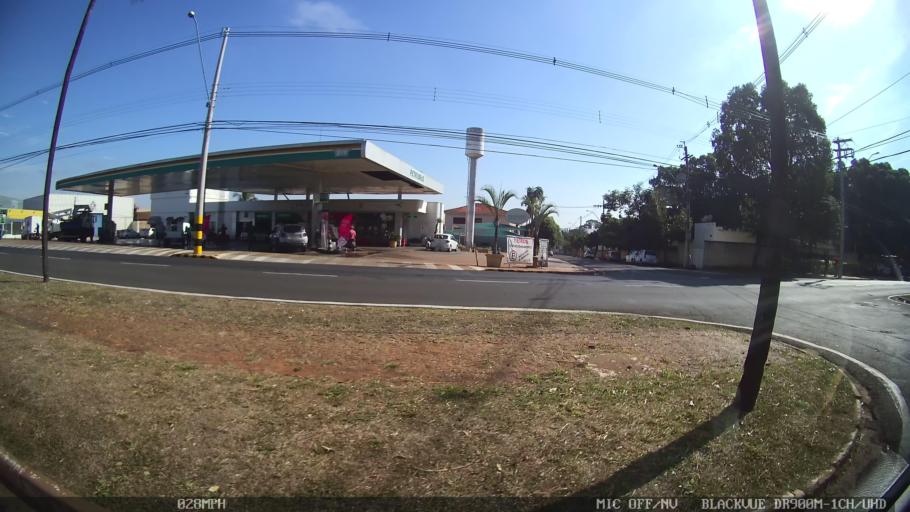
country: BR
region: Sao Paulo
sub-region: Sao Jose Do Rio Preto
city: Sao Jose do Rio Preto
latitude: -20.8113
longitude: -49.4040
